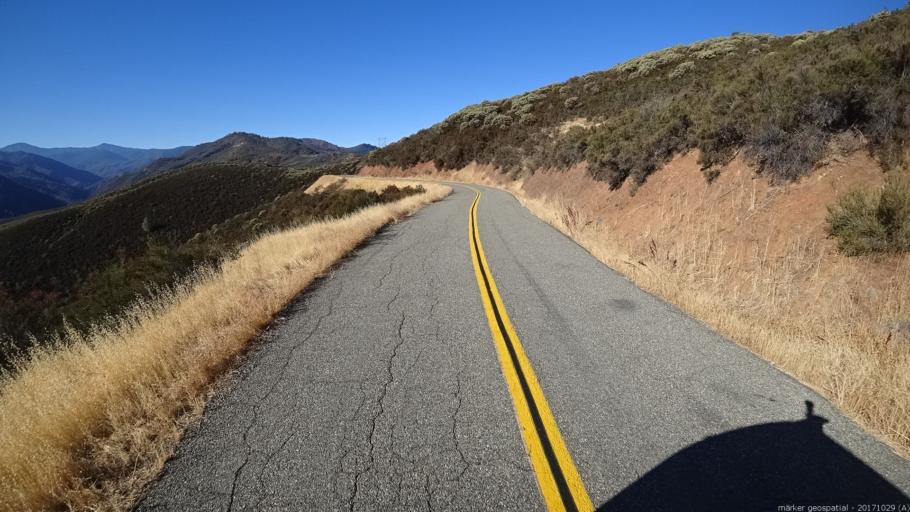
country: US
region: California
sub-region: Trinity County
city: Lewiston
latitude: 40.3652
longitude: -122.8653
